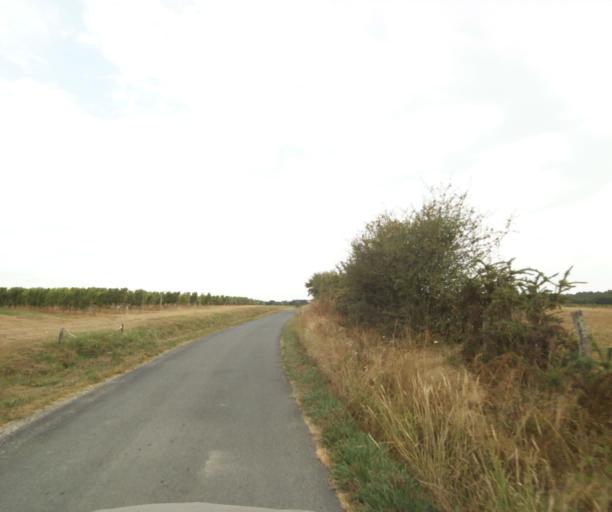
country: FR
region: Aquitaine
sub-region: Departement de la Gironde
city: La Sauve
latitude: 44.7504
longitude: -0.3362
